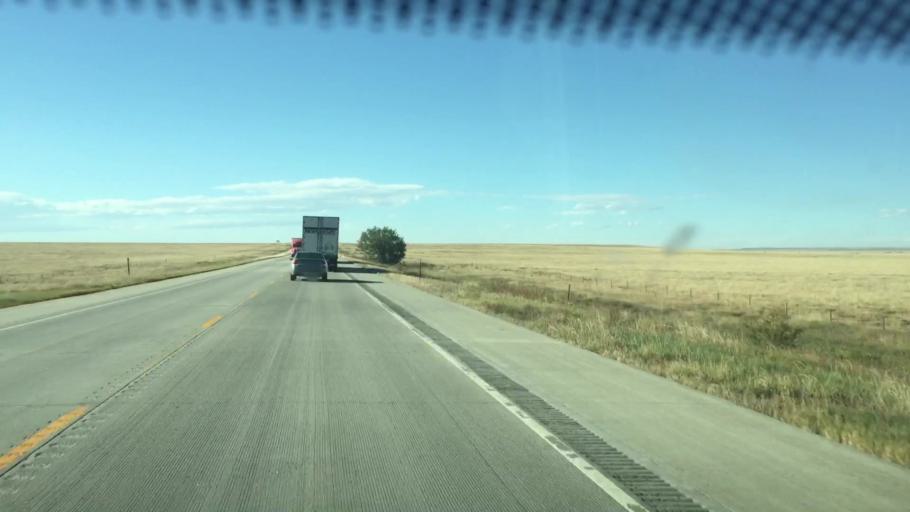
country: US
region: Colorado
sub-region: Lincoln County
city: Hugo
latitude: 38.9184
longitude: -103.1823
